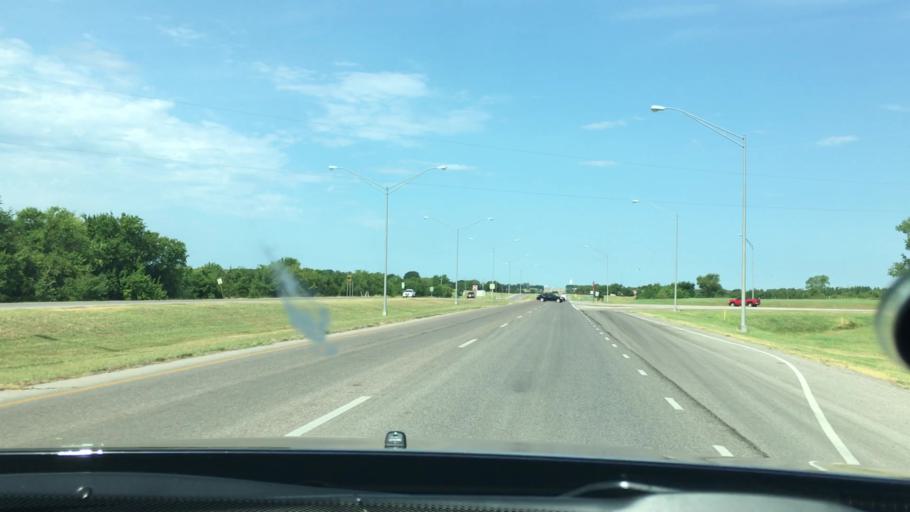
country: US
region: Oklahoma
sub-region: Murray County
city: Sulphur
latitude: 34.5064
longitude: -97.0105
